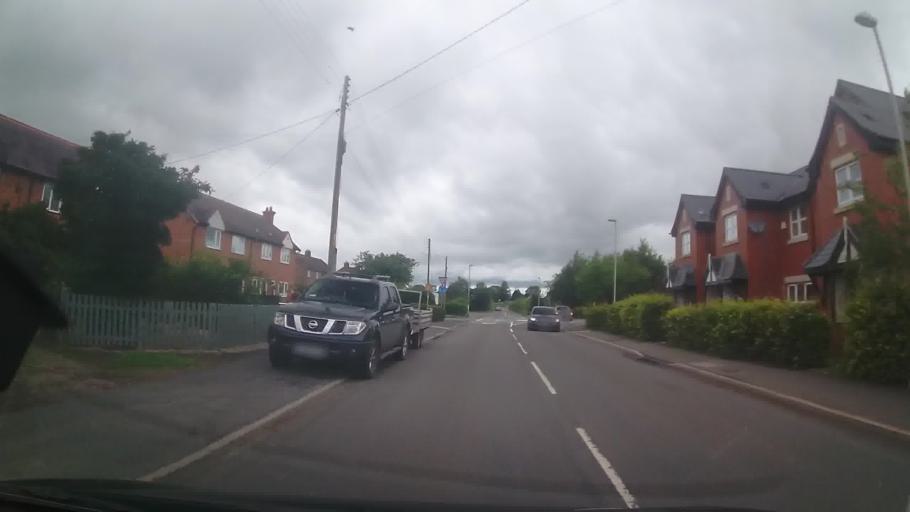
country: GB
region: England
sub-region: Shropshire
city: Petton
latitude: 52.8581
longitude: -2.8424
